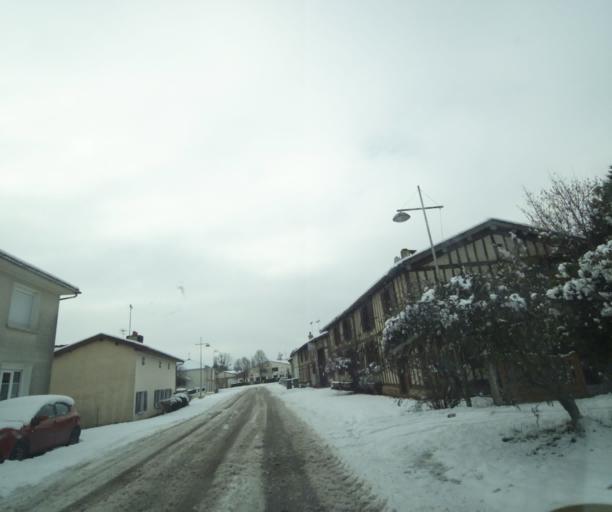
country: FR
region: Champagne-Ardenne
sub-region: Departement de la Haute-Marne
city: Montier-en-Der
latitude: 48.5161
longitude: 4.6997
